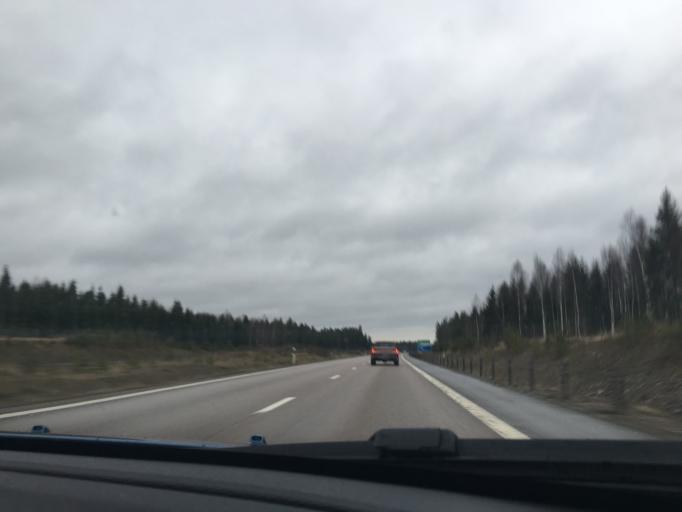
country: SE
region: Uppsala
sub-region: Tierps Kommun
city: Tierp
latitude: 60.4245
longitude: 17.4371
